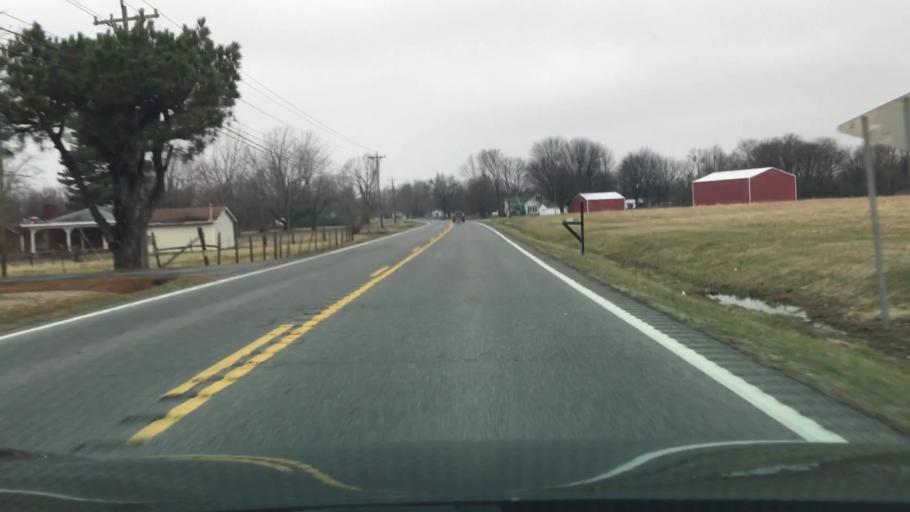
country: US
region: Kentucky
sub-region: Marshall County
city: Calvert City
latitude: 36.9674
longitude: -88.3847
